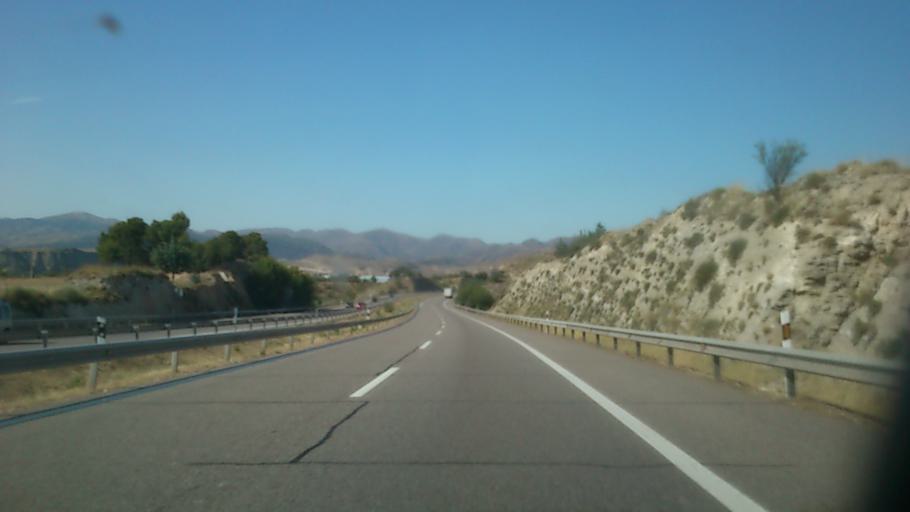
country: ES
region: Aragon
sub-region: Provincia de Zaragoza
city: Calatayud
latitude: 41.3405
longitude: -1.6314
